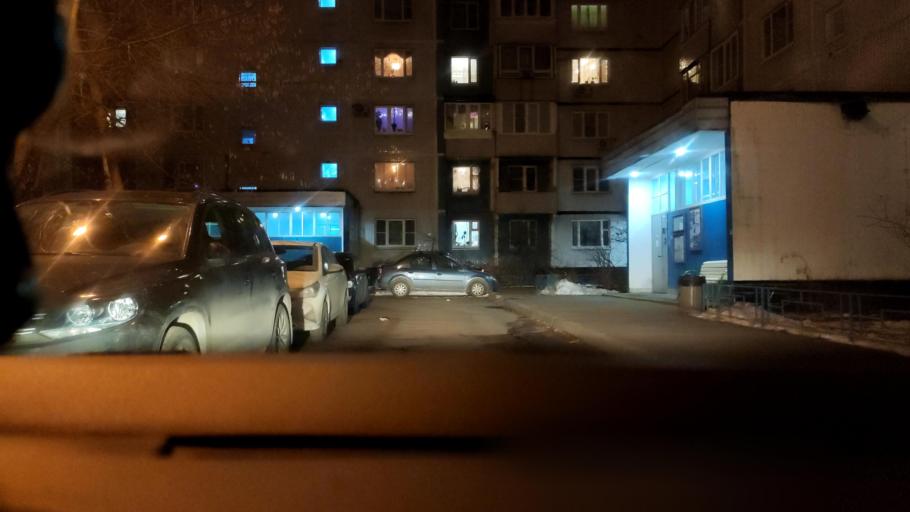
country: RU
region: Moscow
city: Brateyevo
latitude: 55.6399
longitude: 37.7607
